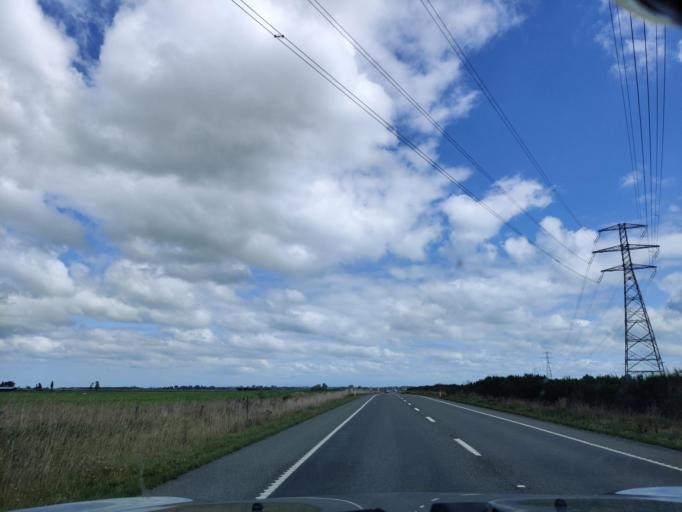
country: NZ
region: Canterbury
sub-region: Timaru District
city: Pleasant Point
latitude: -44.0873
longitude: 171.3365
